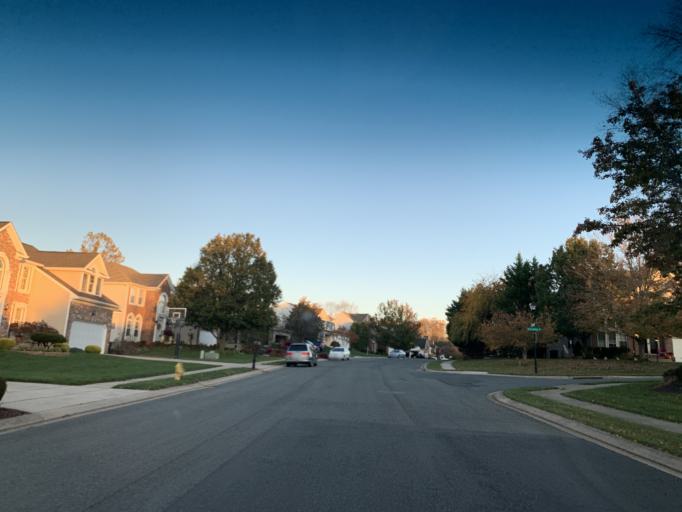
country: US
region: Maryland
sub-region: Harford County
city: South Bel Air
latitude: 39.5499
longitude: -76.3122
